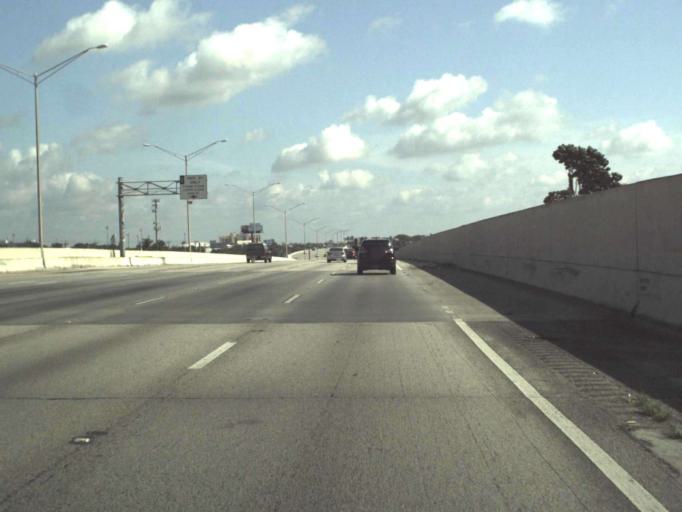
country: US
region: Florida
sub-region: Palm Beach County
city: North Palm Beach
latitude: 26.8230
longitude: -80.0974
